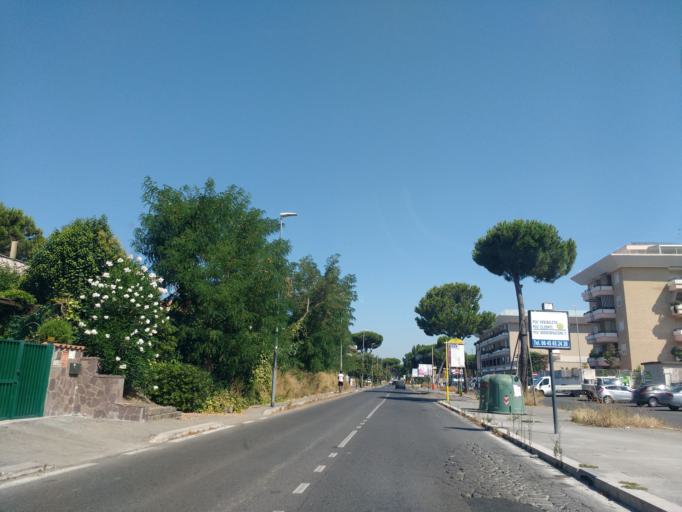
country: IT
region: Latium
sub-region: Citta metropolitana di Roma Capitale
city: Vitinia
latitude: 41.7747
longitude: 12.3705
